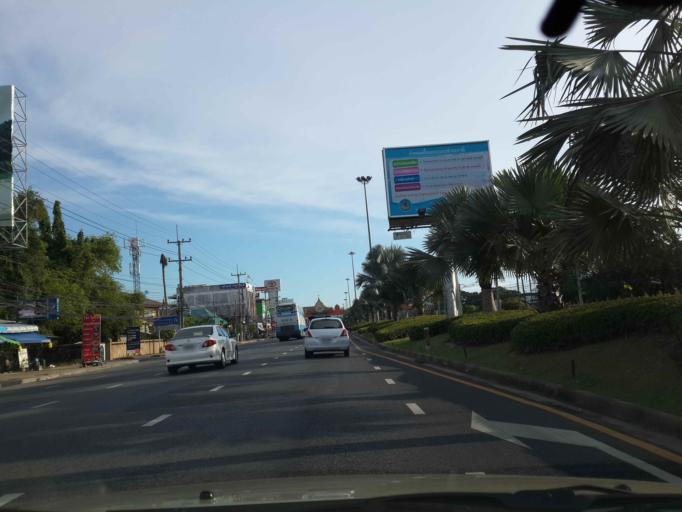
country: TH
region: Chon Buri
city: Phatthaya
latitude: 12.9792
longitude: 100.9172
